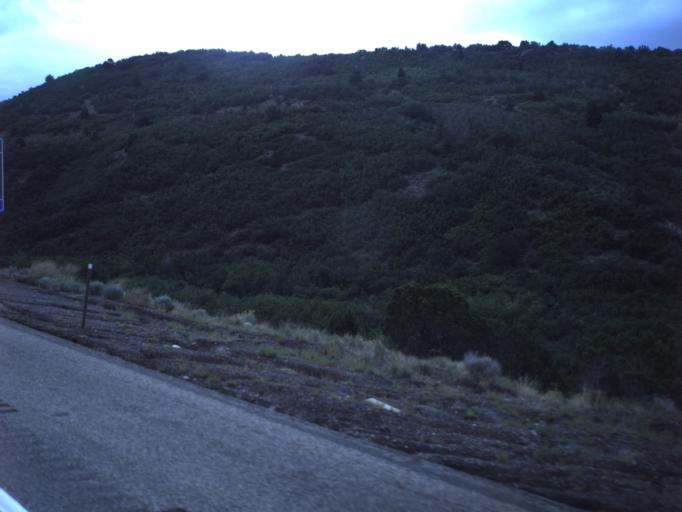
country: US
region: Utah
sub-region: Beaver County
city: Beaver
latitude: 38.5929
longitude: -112.5022
